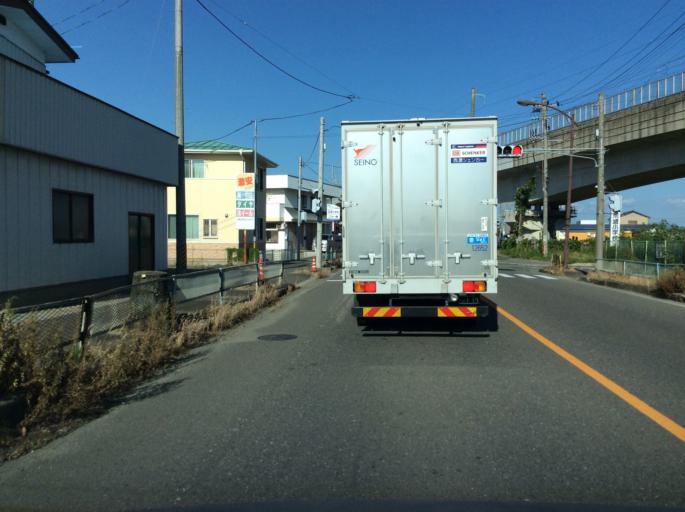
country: JP
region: Fukushima
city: Koriyama
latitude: 37.3662
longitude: 140.3778
